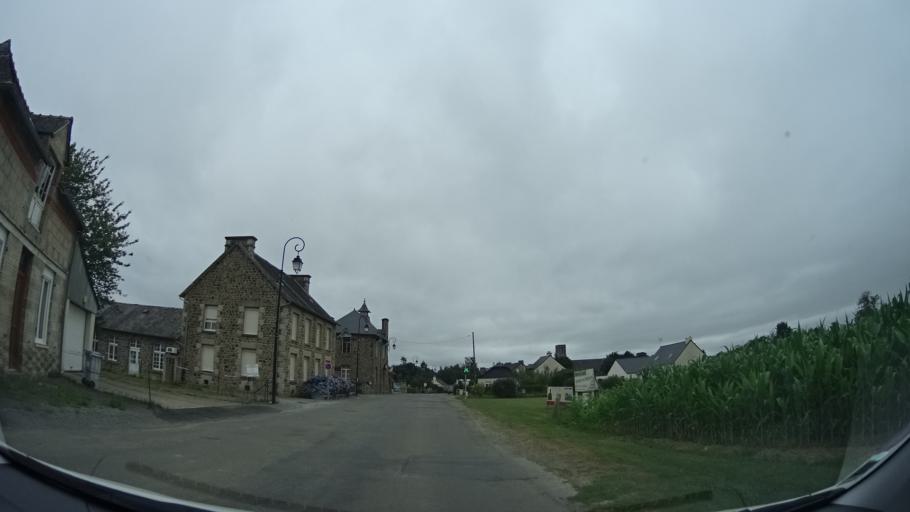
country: FR
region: Brittany
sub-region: Departement des Cotes-d'Armor
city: Evran
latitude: 48.3353
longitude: -1.9337
